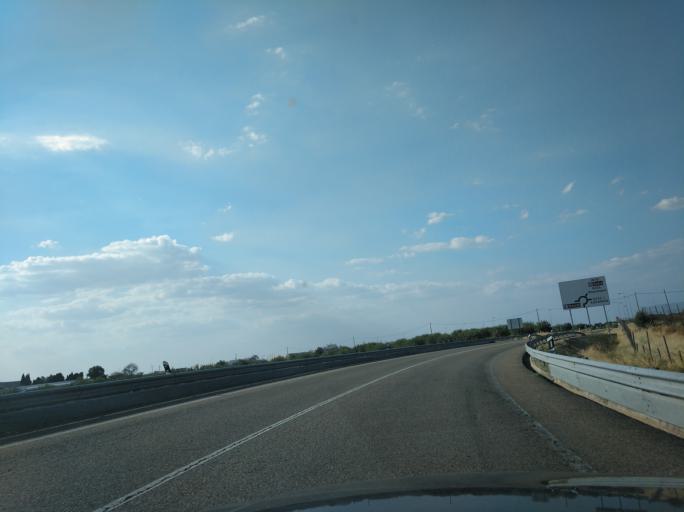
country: PT
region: Evora
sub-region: Mourao
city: Mourao
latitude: 38.3793
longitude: -7.3314
